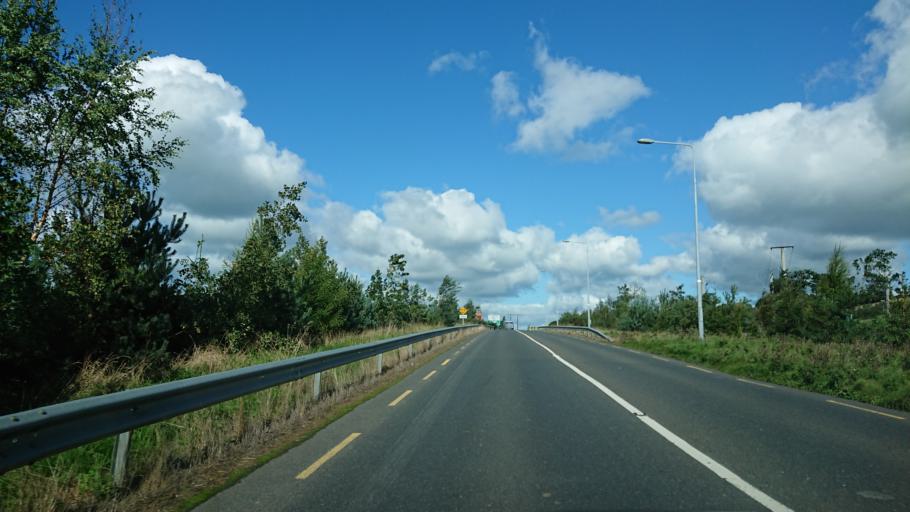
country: IE
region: Leinster
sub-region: Kilkenny
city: Mooncoin
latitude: 52.2388
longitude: -7.2469
